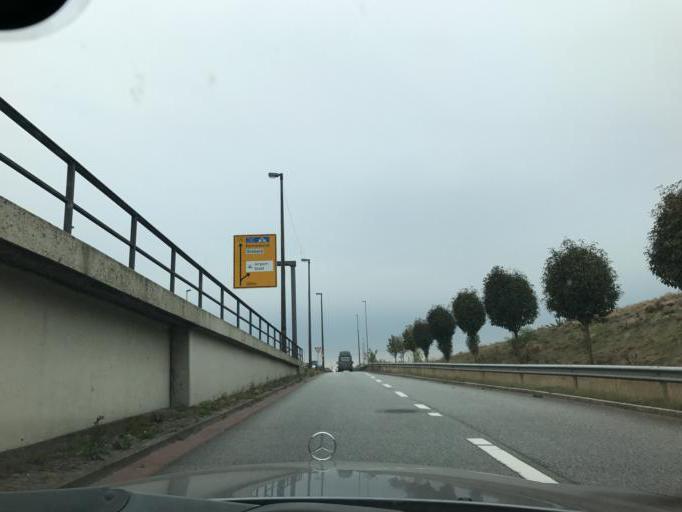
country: DE
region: Bremen
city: Bremen
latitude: 53.0676
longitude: 8.7786
